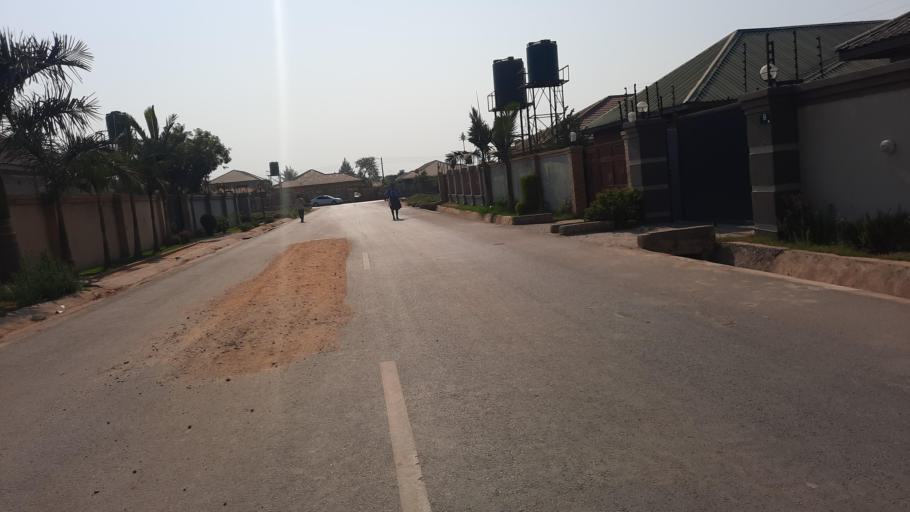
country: ZM
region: Lusaka
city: Lusaka
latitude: -15.3922
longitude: 28.3888
